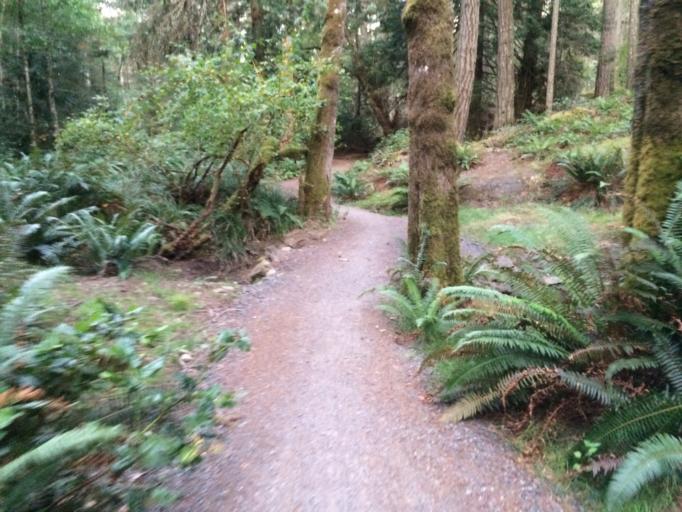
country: CA
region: British Columbia
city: Metchosin
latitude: 48.3530
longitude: -123.5601
